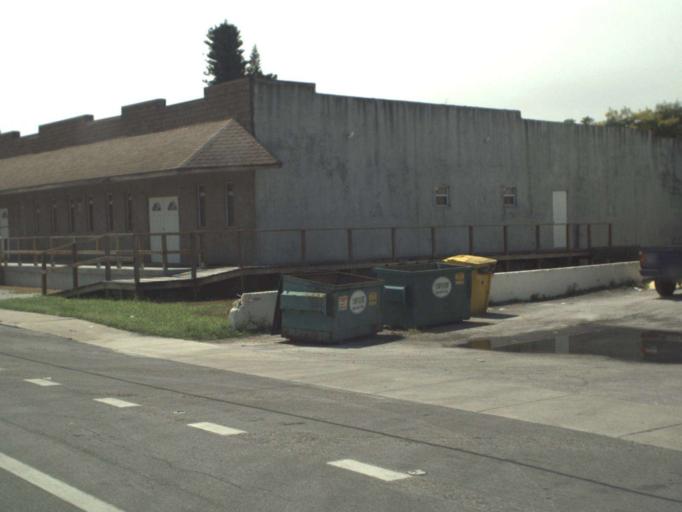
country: US
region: Florida
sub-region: Palm Beach County
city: Pahokee
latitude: 26.8219
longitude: -80.6656
